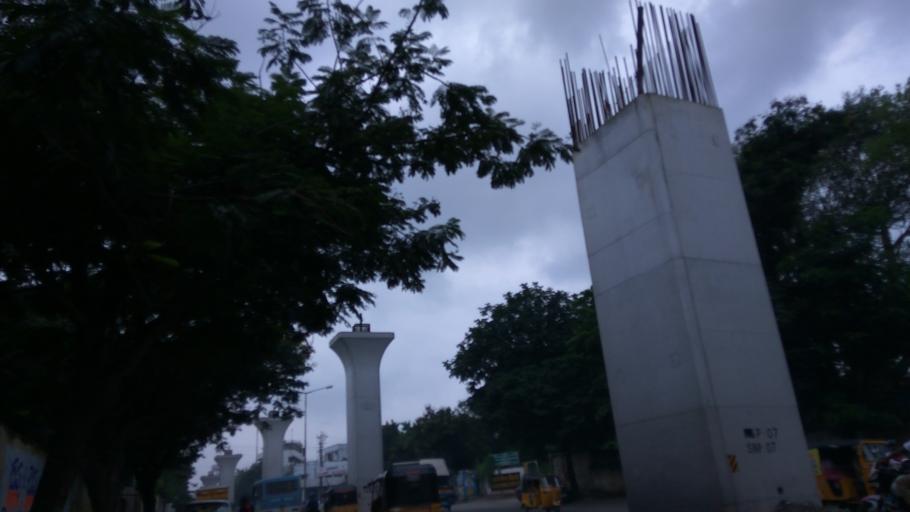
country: IN
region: Telangana
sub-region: Hyderabad
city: Malkajgiri
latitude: 17.4321
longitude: 78.5059
